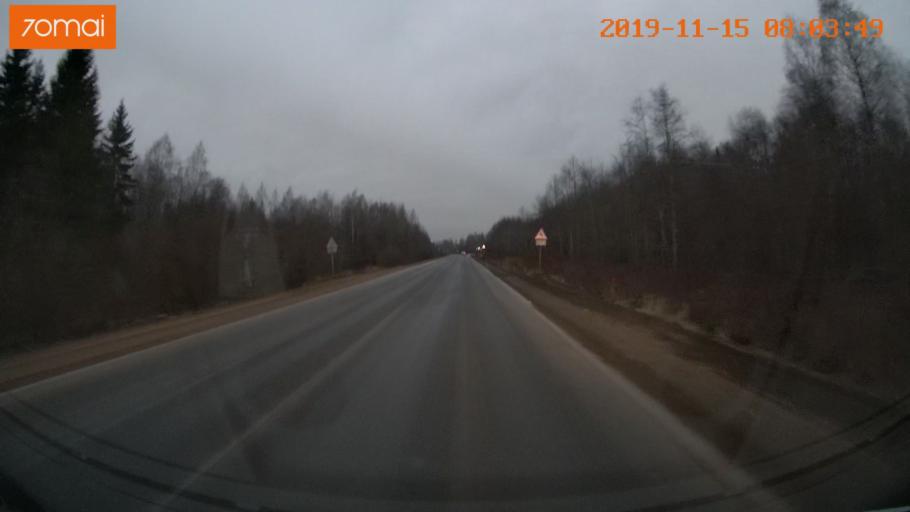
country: RU
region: Vologda
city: Cherepovets
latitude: 59.0019
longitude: 38.0843
